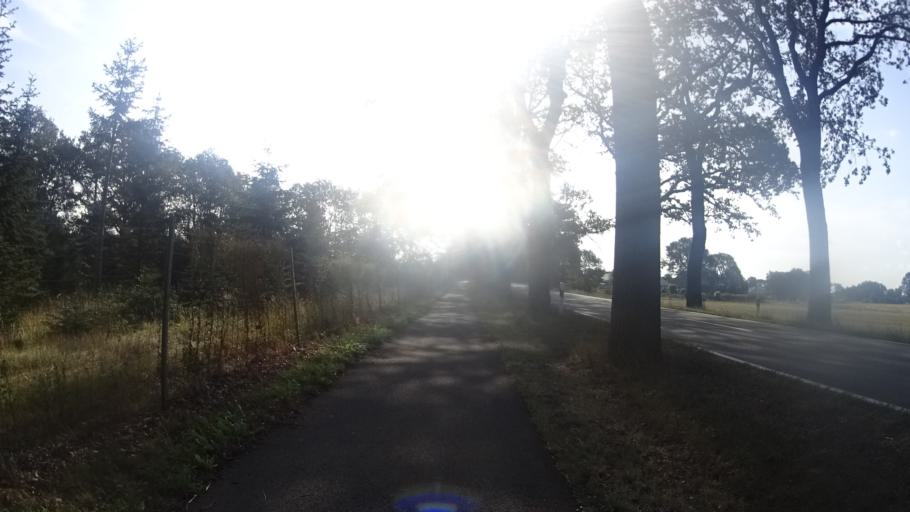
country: DE
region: Brandenburg
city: Cumlosen
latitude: 53.0272
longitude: 11.6664
